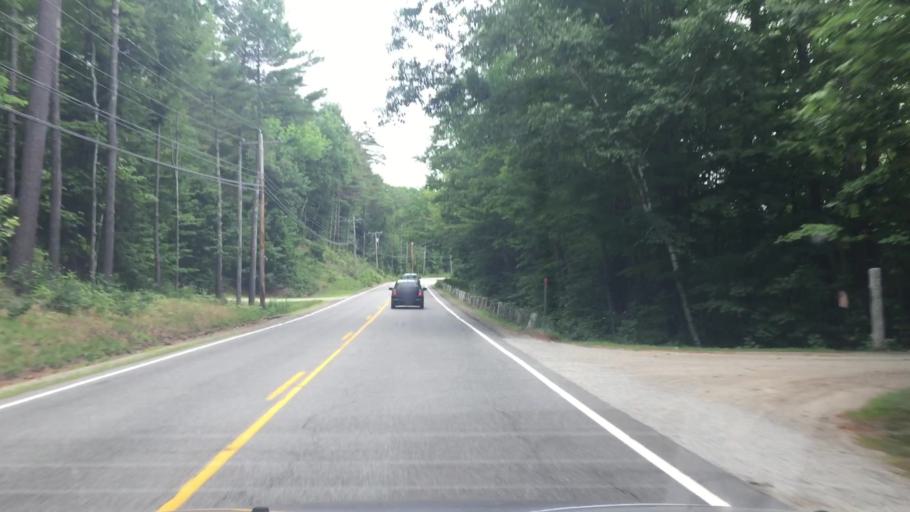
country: US
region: New Hampshire
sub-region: Carroll County
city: Moultonborough
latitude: 43.7395
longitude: -71.4135
